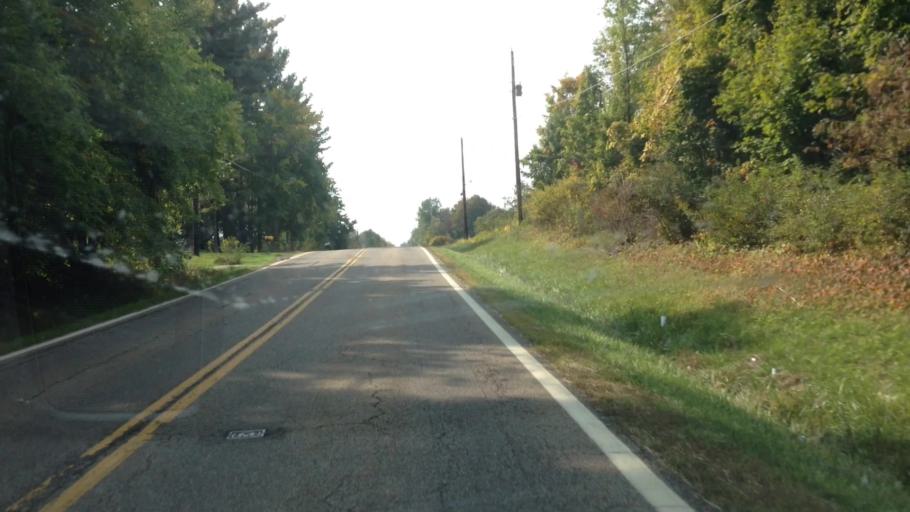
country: US
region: Ohio
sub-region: Medina County
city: Lodi
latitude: 41.0991
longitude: -82.0089
